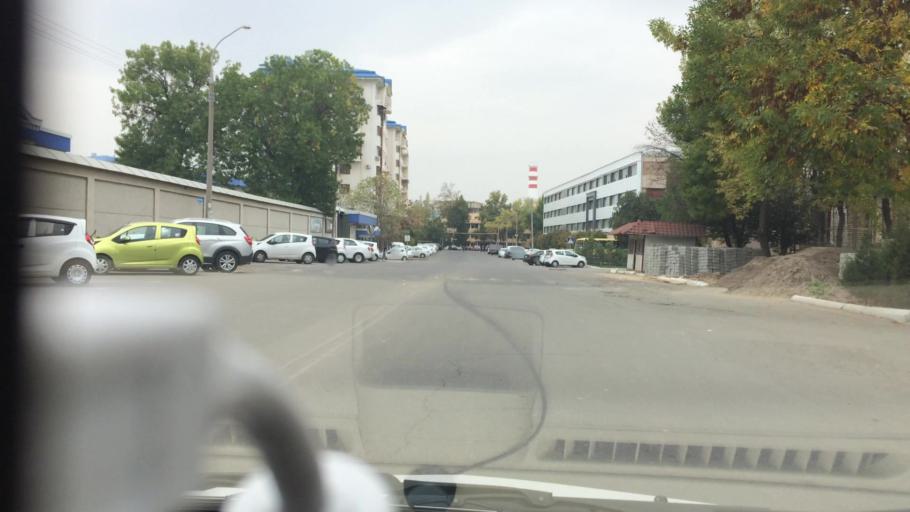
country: UZ
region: Toshkent Shahri
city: Tashkent
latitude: 41.2785
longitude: 69.2657
